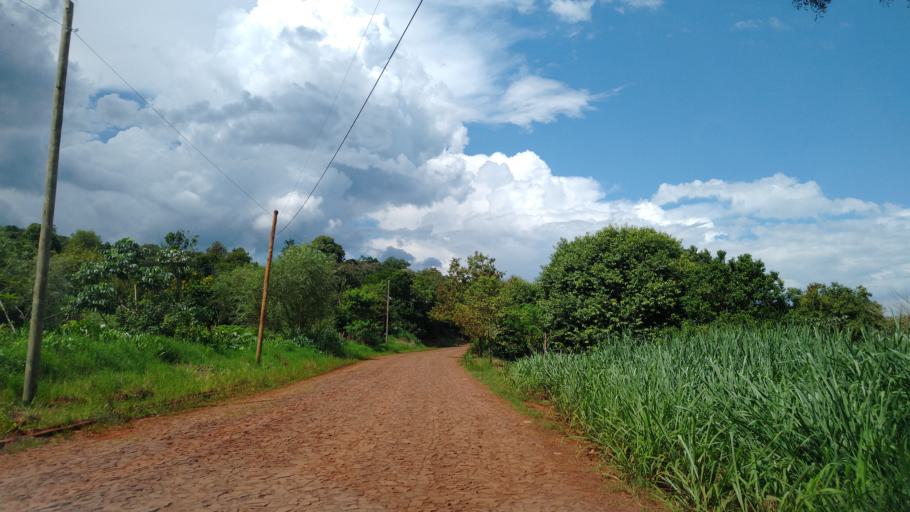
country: AR
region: Misiones
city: Puerto Libertad
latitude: -25.9658
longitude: -54.6012
